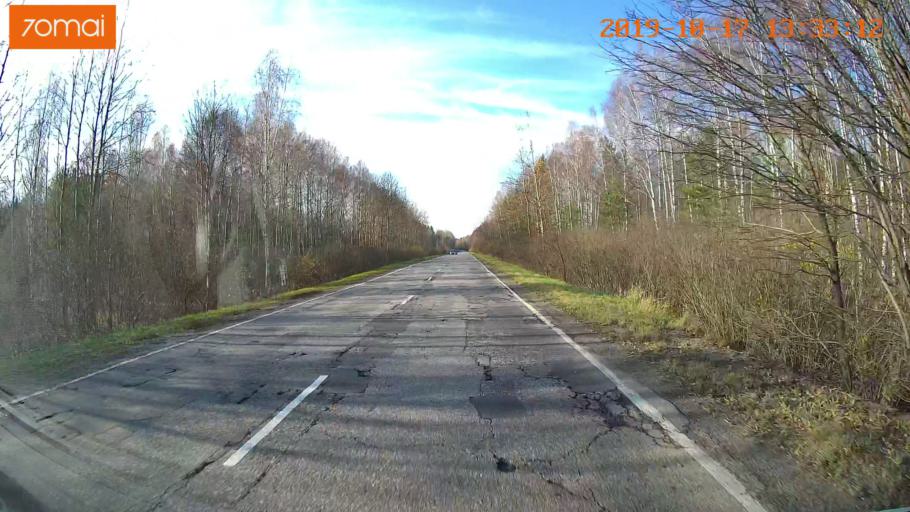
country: RU
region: Vladimir
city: Velikodvorskiy
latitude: 55.1413
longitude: 40.7468
